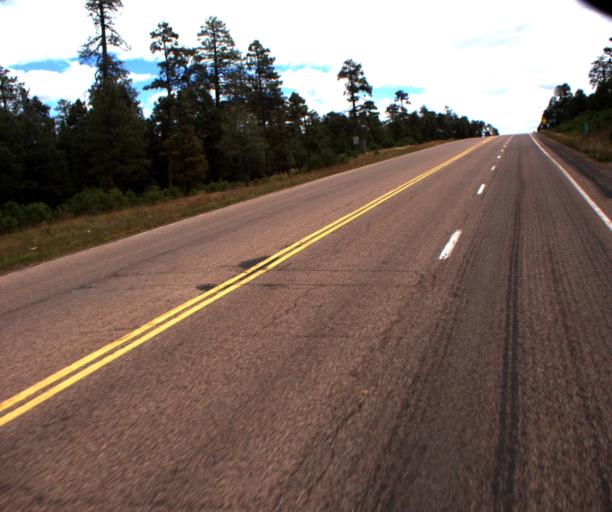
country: US
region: Arizona
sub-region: Navajo County
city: Heber-Overgaard
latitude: 34.3331
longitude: -110.7561
